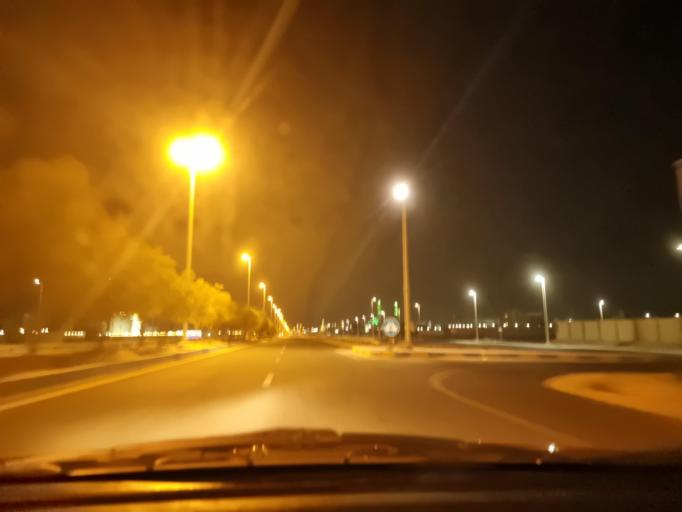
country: AE
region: Abu Dhabi
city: Abu Dhabi
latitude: 24.3706
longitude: 54.7029
